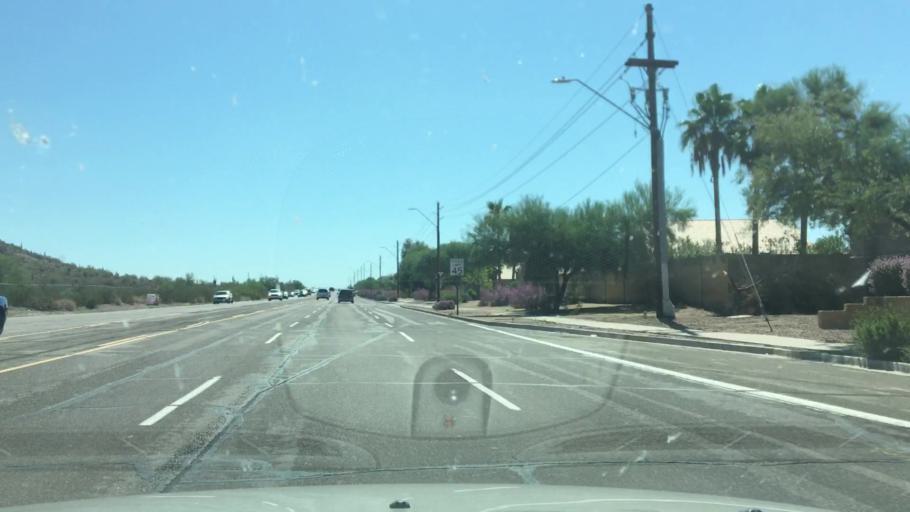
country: US
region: Arizona
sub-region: Maricopa County
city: Sun City
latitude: 33.7122
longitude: -112.1957
